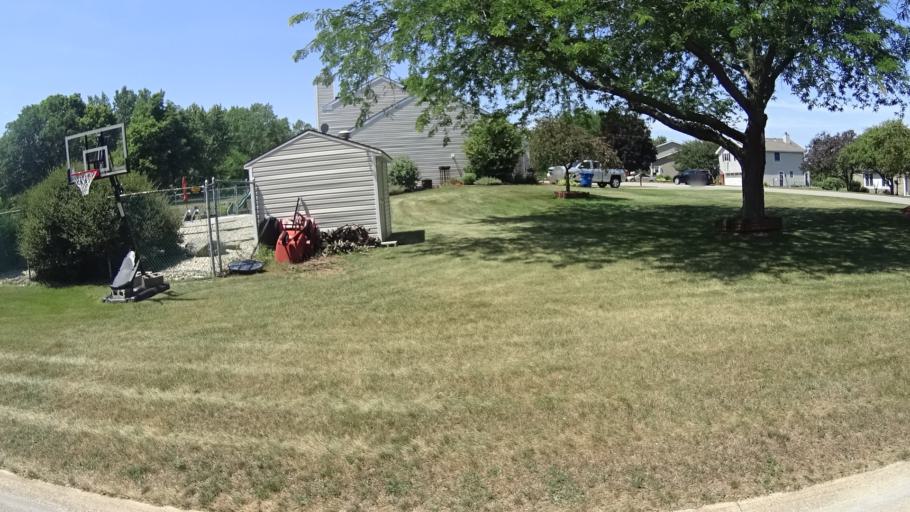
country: US
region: Ohio
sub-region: Erie County
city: Sandusky
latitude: 41.4029
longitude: -82.7904
